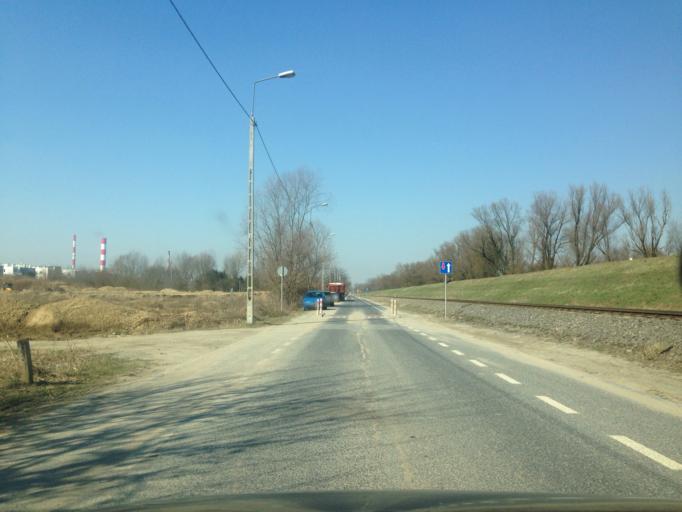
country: PL
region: Masovian Voivodeship
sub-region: Warszawa
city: Wilanow
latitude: 52.1736
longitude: 21.1196
